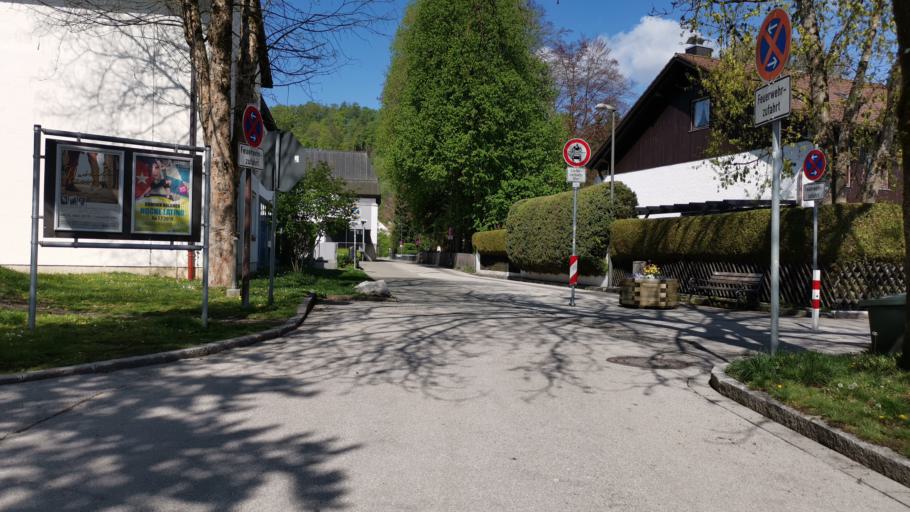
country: DE
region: Bavaria
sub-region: Upper Bavaria
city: Wolfratshausen
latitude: 47.9137
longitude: 11.4227
